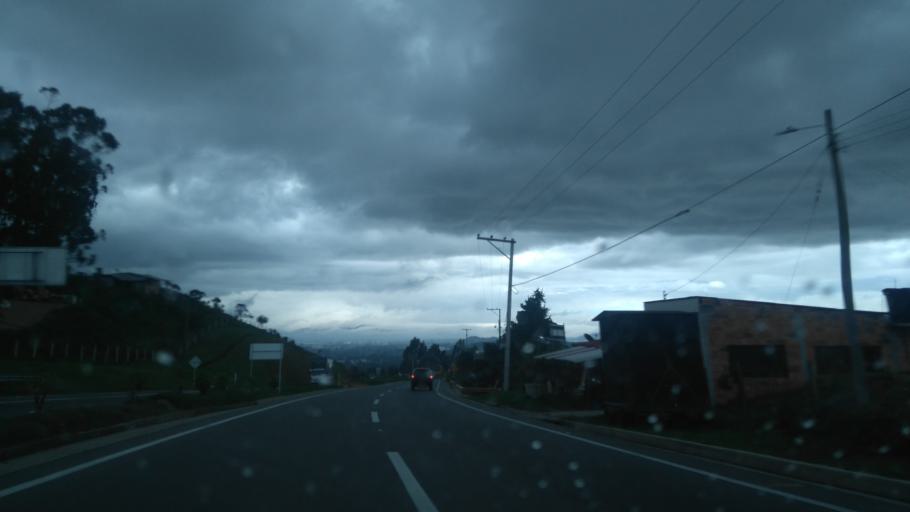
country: CO
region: Cundinamarca
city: El Rosal
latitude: 4.8613
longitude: -74.2899
